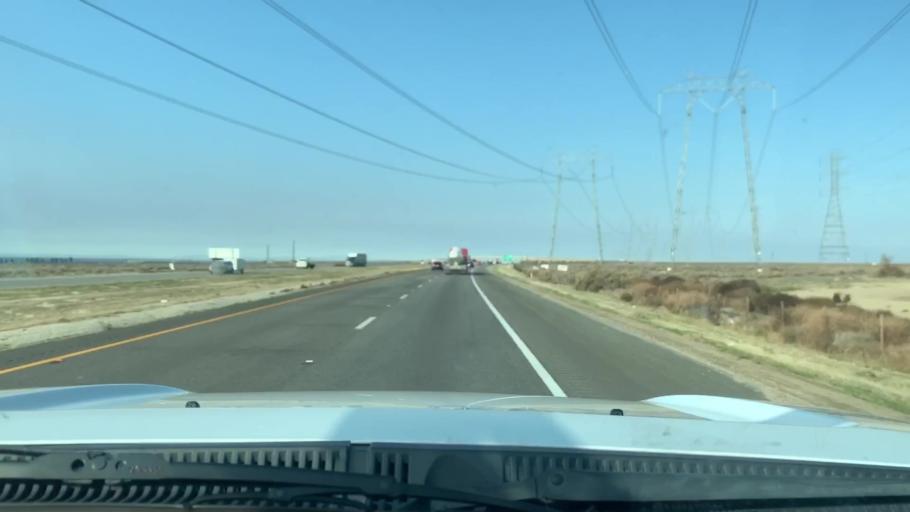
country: US
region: California
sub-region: Kern County
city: Buttonwillow
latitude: 35.4942
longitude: -119.5280
